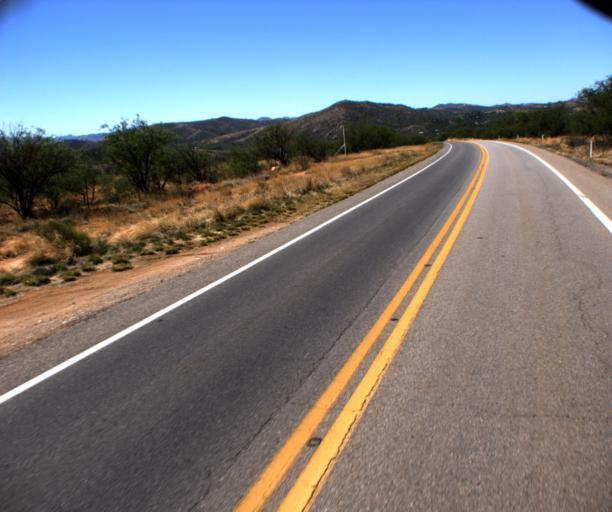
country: US
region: Arizona
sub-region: Santa Cruz County
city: Nogales
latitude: 31.4057
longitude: -110.8662
